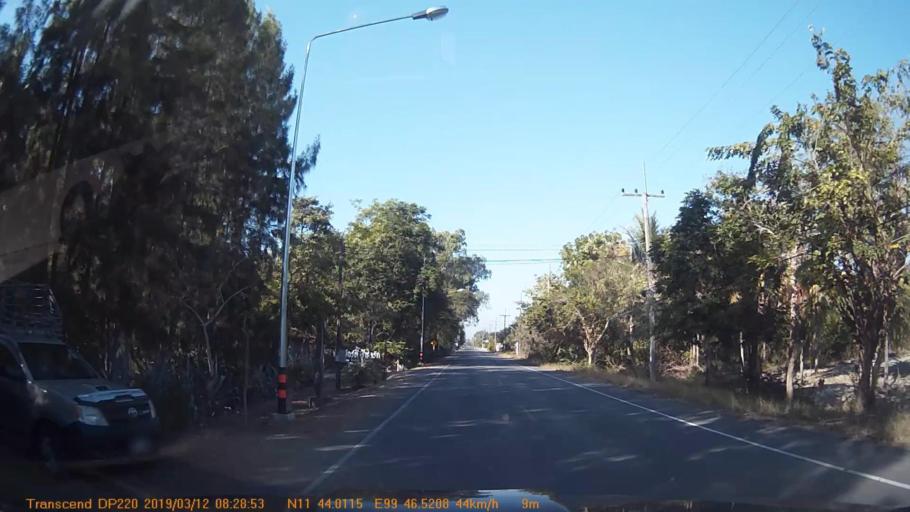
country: TH
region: Prachuap Khiri Khan
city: Prachuap Khiri Khan
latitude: 11.7334
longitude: 99.7752
